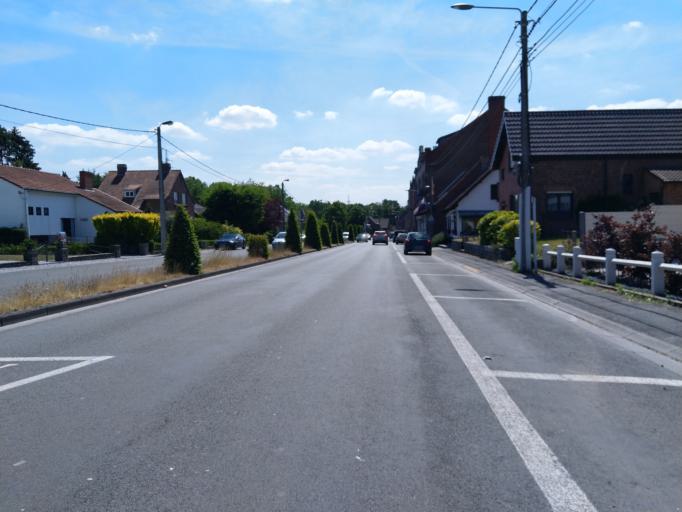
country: BE
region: Wallonia
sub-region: Province du Hainaut
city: Saint-Ghislain
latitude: 50.4814
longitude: 3.8323
